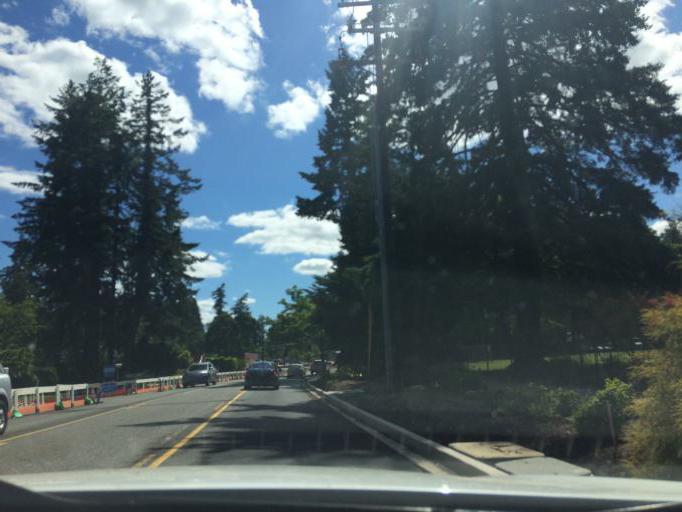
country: US
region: Oregon
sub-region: Washington County
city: Durham
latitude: 45.4120
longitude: -122.7177
